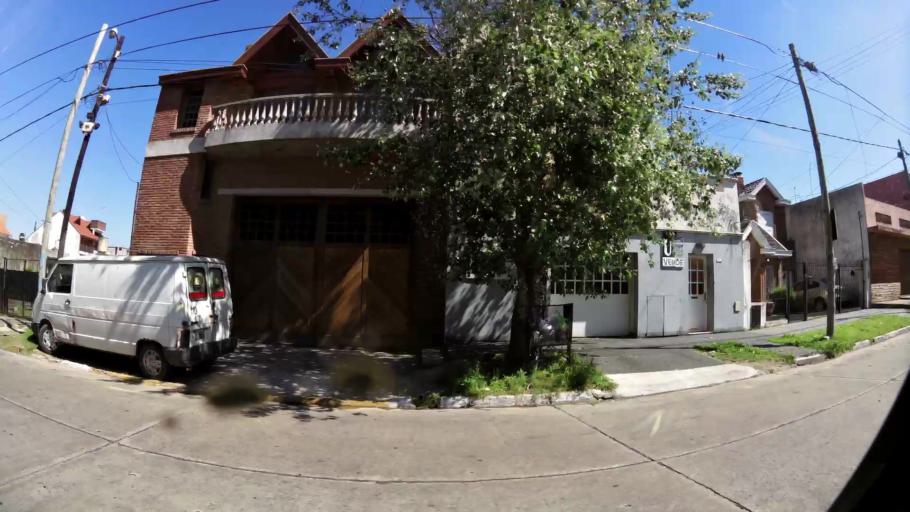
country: AR
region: Buenos Aires
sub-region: Partido de Quilmes
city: Quilmes
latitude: -34.7132
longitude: -58.2955
